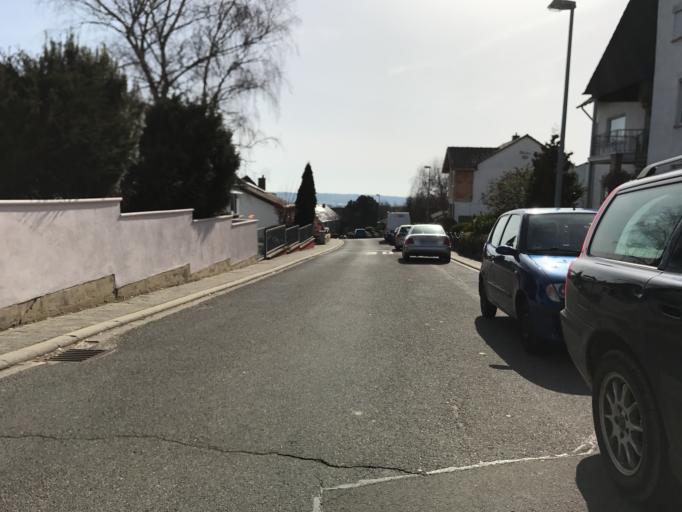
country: DE
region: Rheinland-Pfalz
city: Essenheim
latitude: 49.9288
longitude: 8.1524
